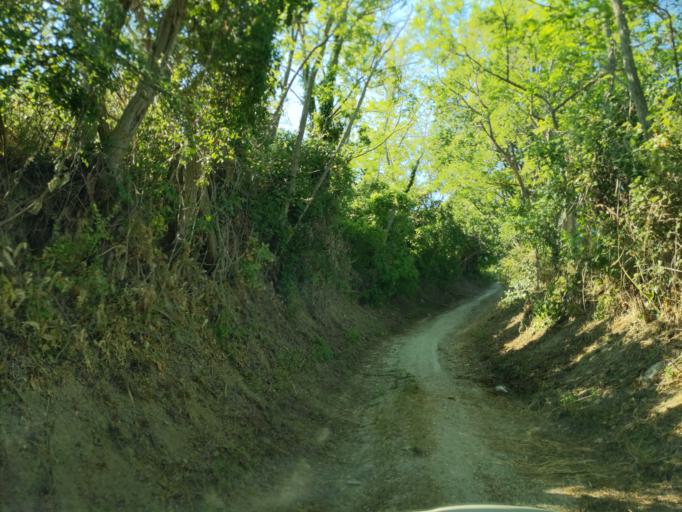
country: IT
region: The Marches
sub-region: Provincia di Pesaro e Urbino
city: Cuccurano
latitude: 43.8033
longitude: 12.9626
